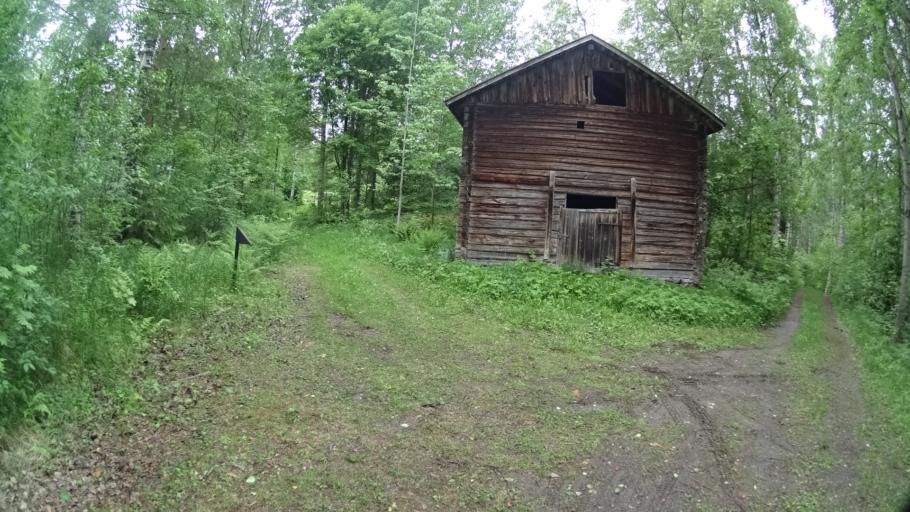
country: FI
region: Southern Savonia
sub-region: Savonlinna
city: Savonlinna
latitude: 61.9215
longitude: 28.8262
